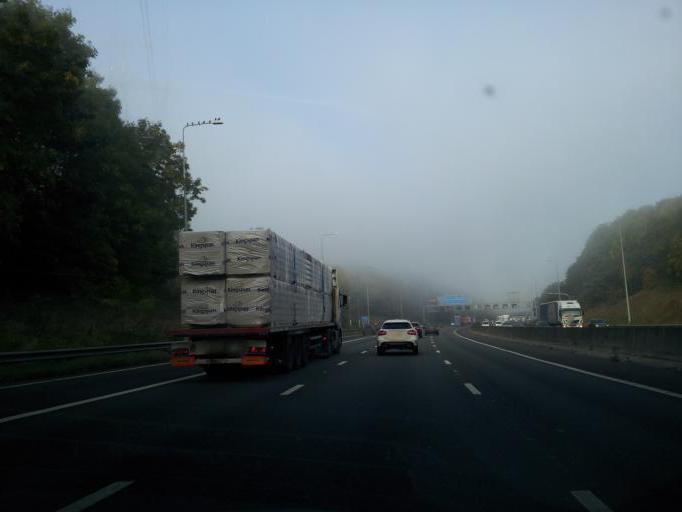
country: GB
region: England
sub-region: Kirklees
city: Cleckheaton
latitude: 53.7416
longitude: -1.6913
